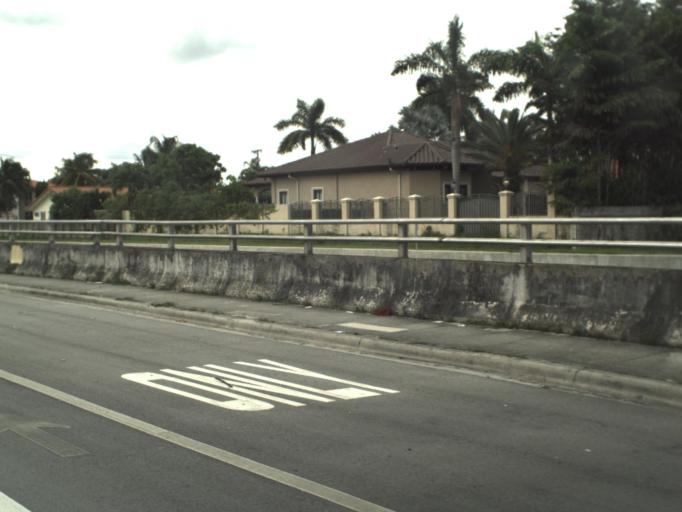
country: US
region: Florida
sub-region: Miami-Dade County
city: Tamiami
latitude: 25.7611
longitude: -80.3936
